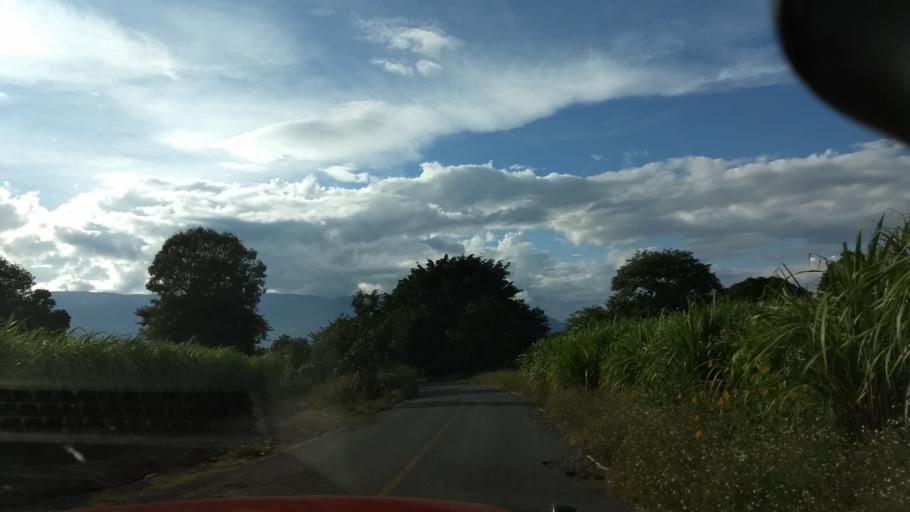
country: MX
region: Colima
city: Suchitlan
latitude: 19.4679
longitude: -103.7642
